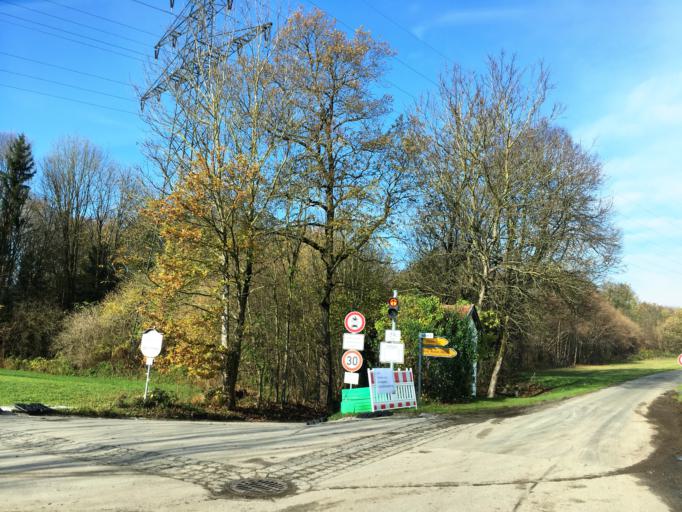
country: DE
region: Bavaria
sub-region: Upper Bavaria
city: Rosenheim
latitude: 47.8882
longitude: 12.1494
